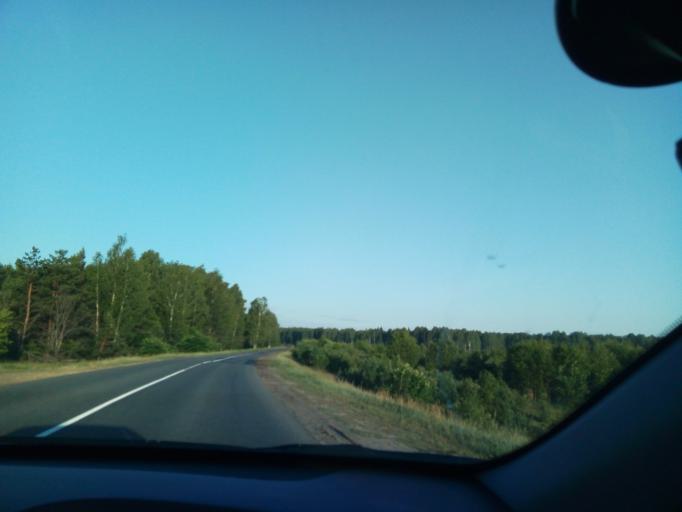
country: RU
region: Nizjnij Novgorod
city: Satis
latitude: 54.9299
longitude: 43.2040
